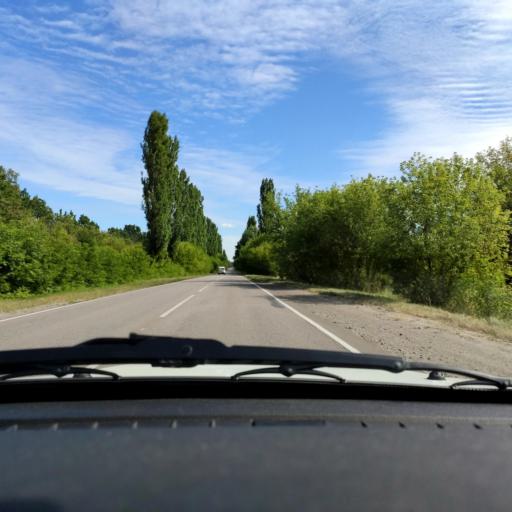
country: RU
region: Voronezj
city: Uglyanets
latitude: 51.8332
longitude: 39.6487
